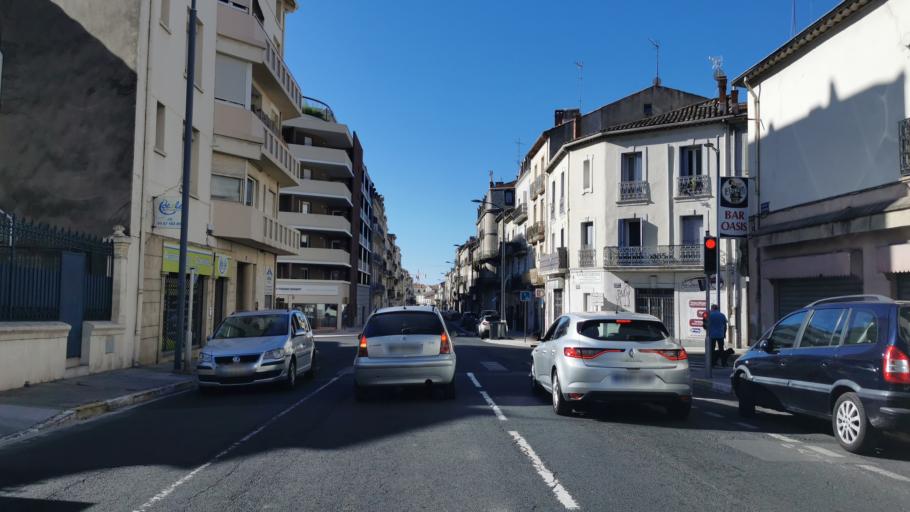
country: FR
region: Languedoc-Roussillon
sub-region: Departement de l'Herault
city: Beziers
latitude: 43.3443
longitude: 3.2203
